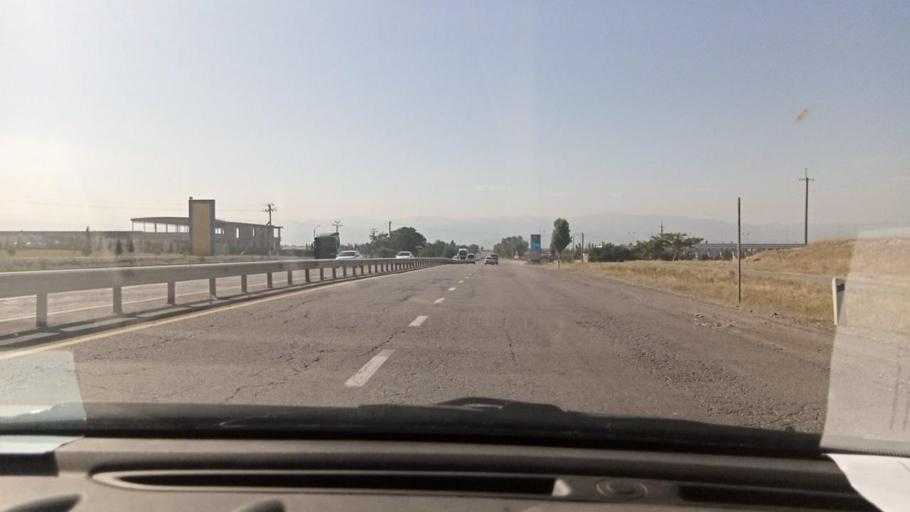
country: UZ
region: Toshkent
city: Ohangaron
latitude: 40.9412
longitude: 69.5816
